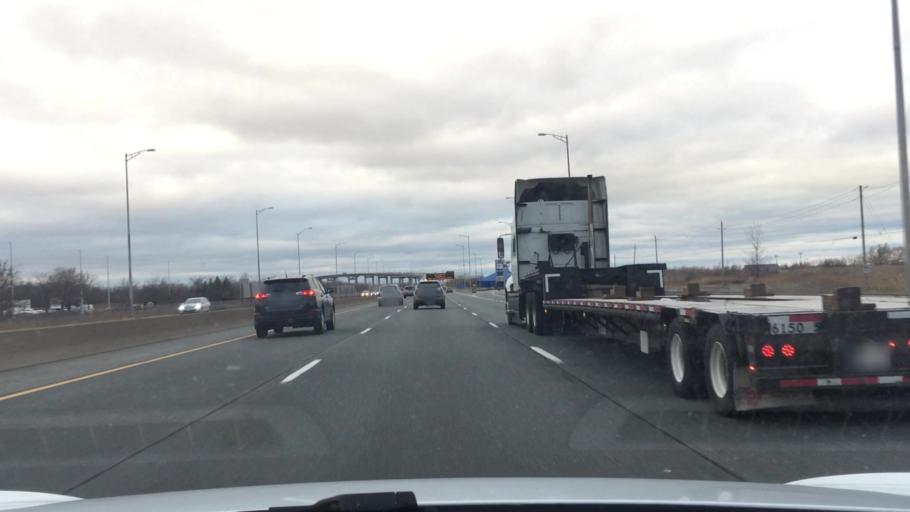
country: CA
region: Ontario
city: Thorold
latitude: 43.1609
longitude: -79.1764
